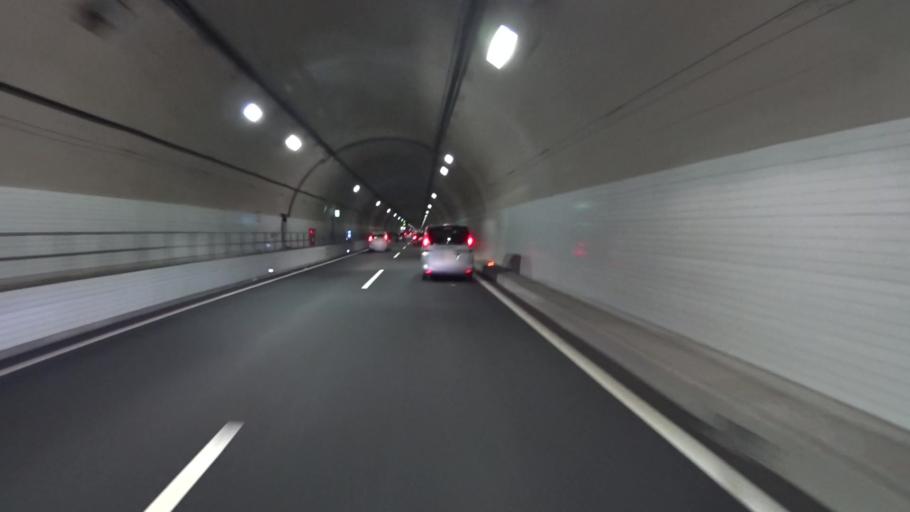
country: JP
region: Kyoto
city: Muko
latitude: 34.9264
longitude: 135.6660
